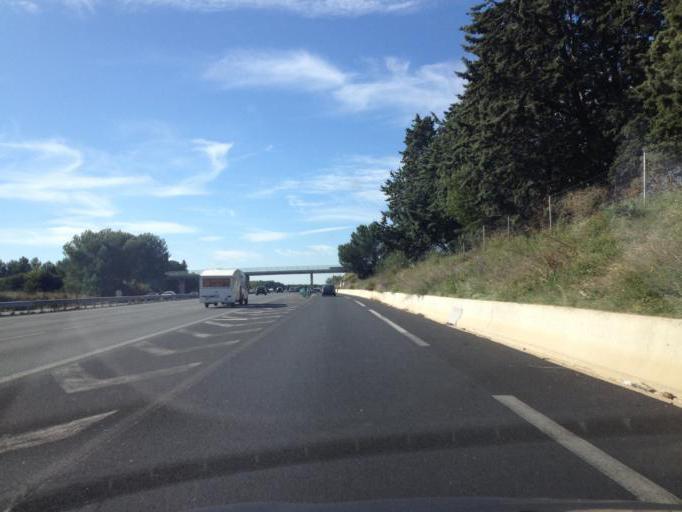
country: FR
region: Languedoc-Roussillon
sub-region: Departement de l'Herault
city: Le Cres
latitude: 43.6118
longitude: 3.9405
